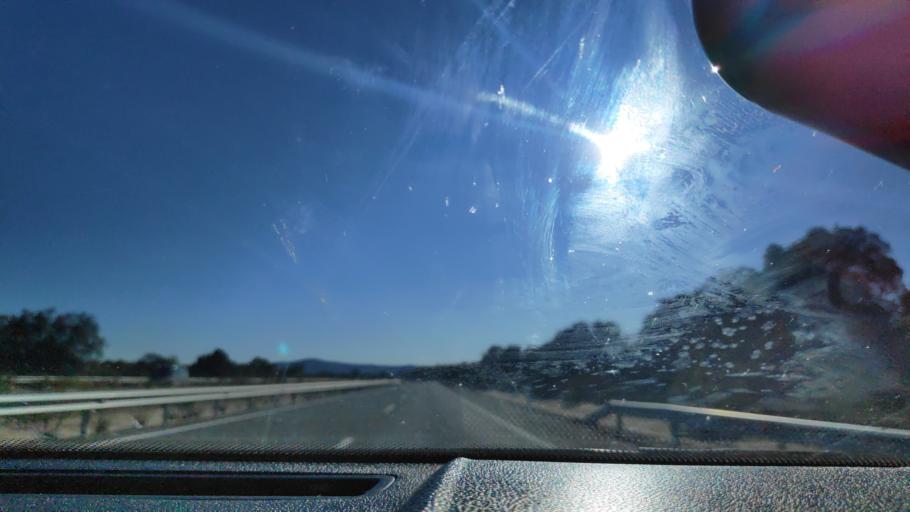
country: ES
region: Extremadura
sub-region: Provincia de Badajoz
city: Monesterio
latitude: 38.0142
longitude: -6.2273
